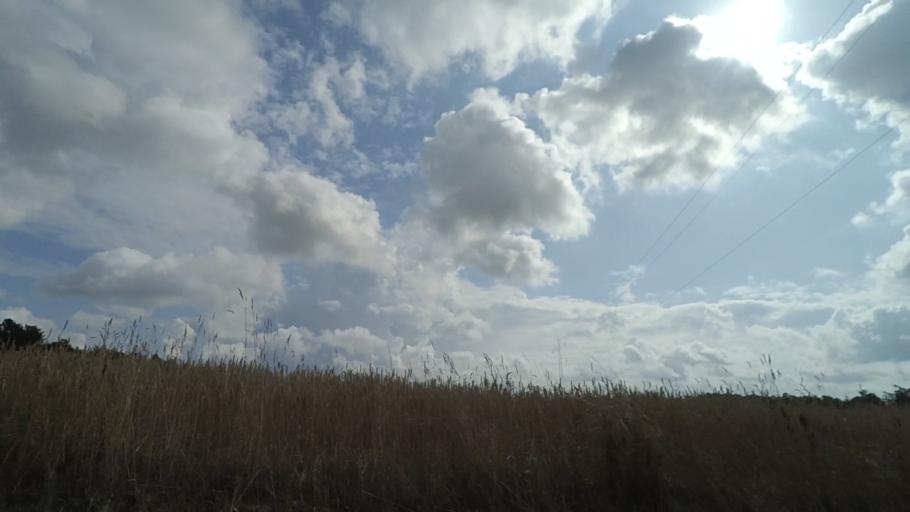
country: DK
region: Central Jutland
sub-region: Syddjurs Kommune
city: Ryomgard
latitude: 56.4830
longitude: 10.4845
